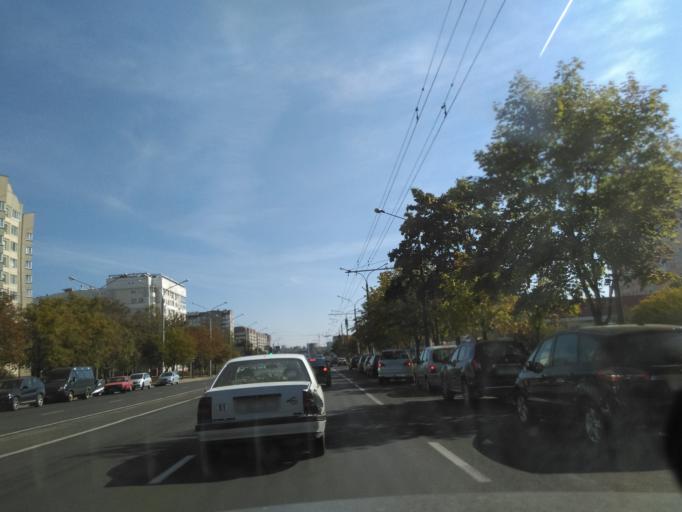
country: BY
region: Minsk
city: Minsk
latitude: 53.8614
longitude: 27.6015
